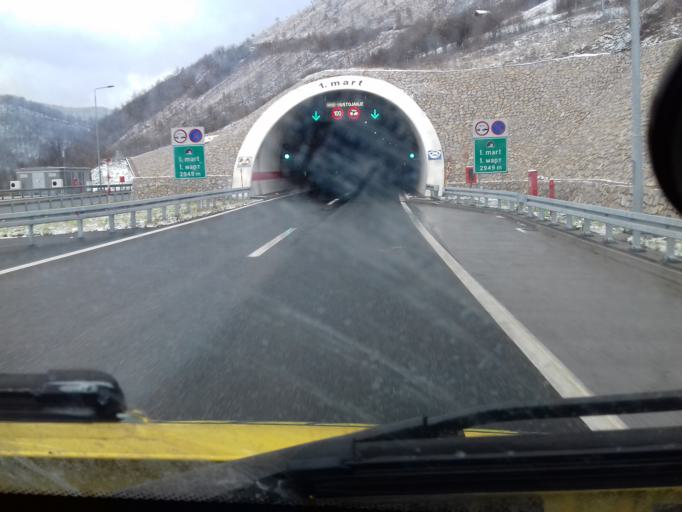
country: BA
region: Federation of Bosnia and Herzegovina
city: Kacuni
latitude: 44.1333
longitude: 17.9863
